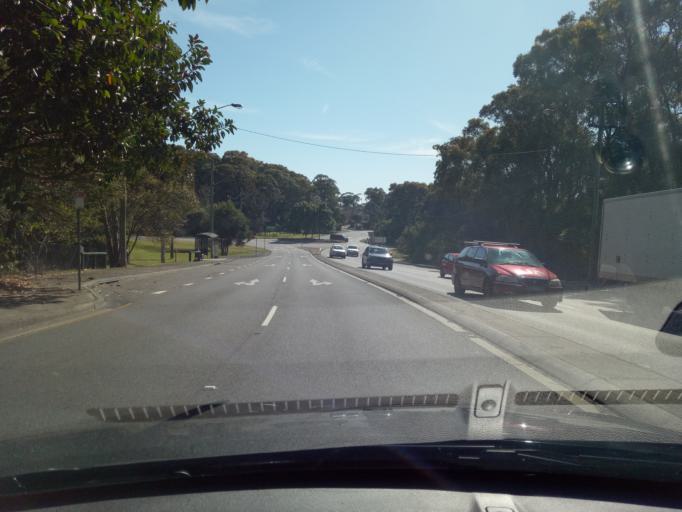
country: AU
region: New South Wales
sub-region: Gosford Shire
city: Forresters Beach
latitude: -33.4156
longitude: 151.4498
